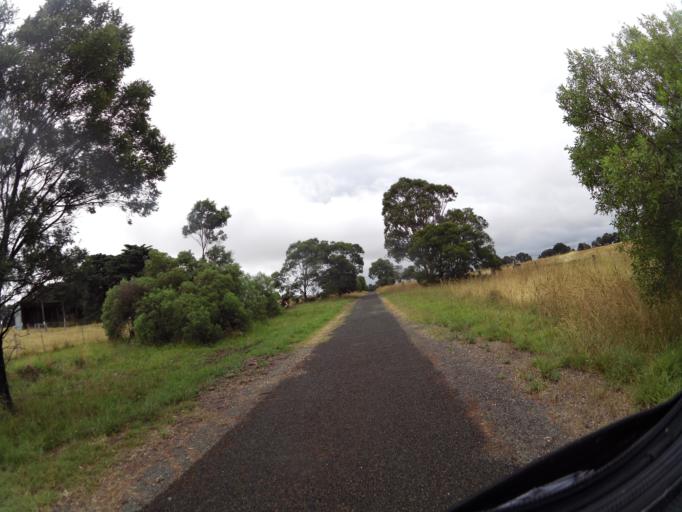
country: AU
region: Victoria
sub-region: East Gippsland
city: Bairnsdale
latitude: -37.8238
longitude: 147.7050
